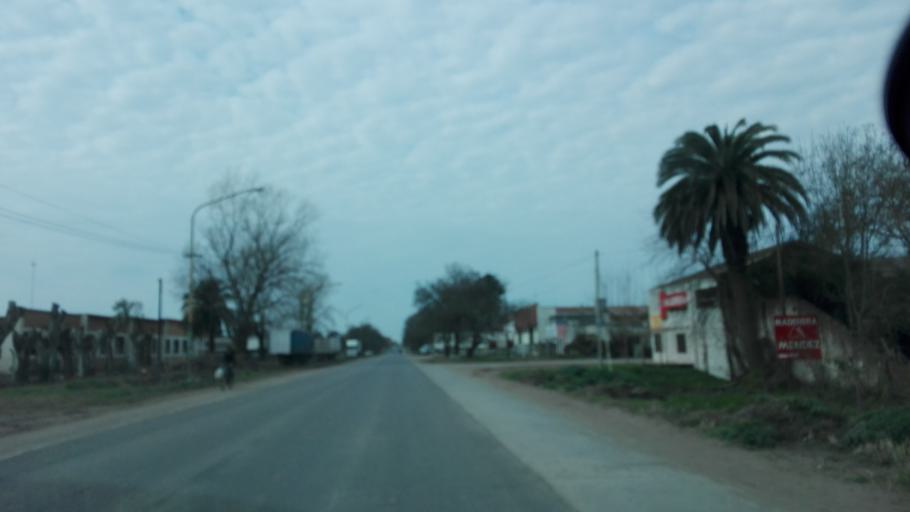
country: AR
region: Buenos Aires
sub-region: Partido de Chascomus
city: Chascomus
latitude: -35.5752
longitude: -57.9934
